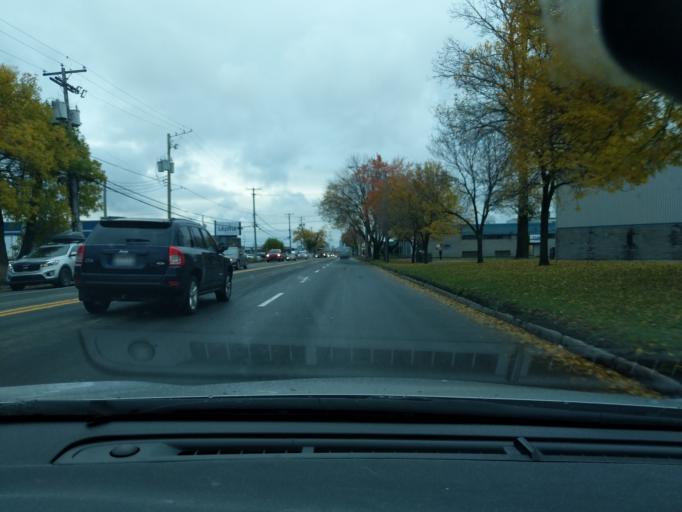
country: CA
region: Quebec
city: L'Ancienne-Lorette
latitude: 46.8063
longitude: -71.3043
